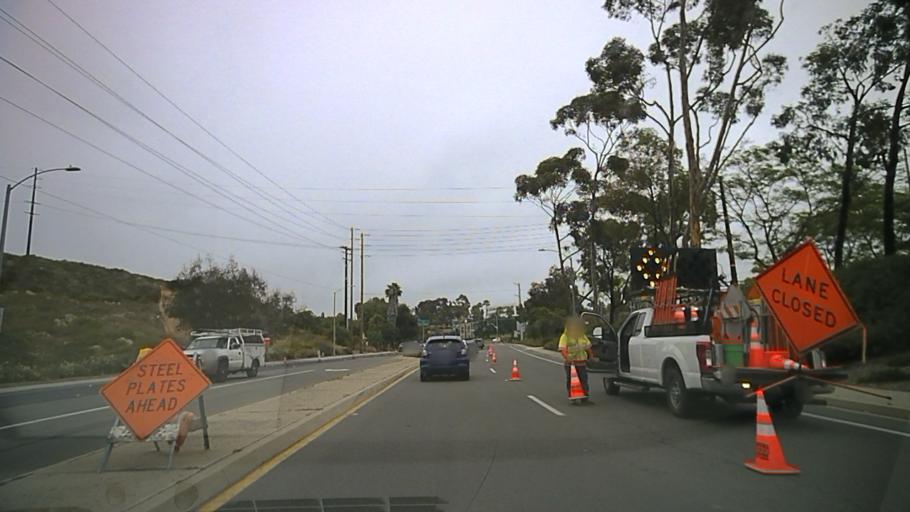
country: US
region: California
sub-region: San Diego County
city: Fairbanks Ranch
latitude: 33.0219
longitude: -117.1031
